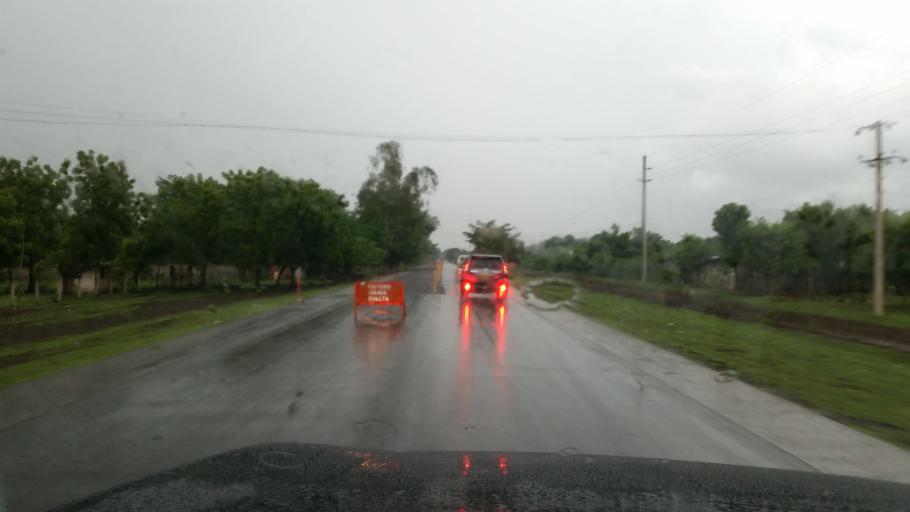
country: NI
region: Chinandega
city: Chichigalpa
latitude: 12.7890
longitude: -86.9523
